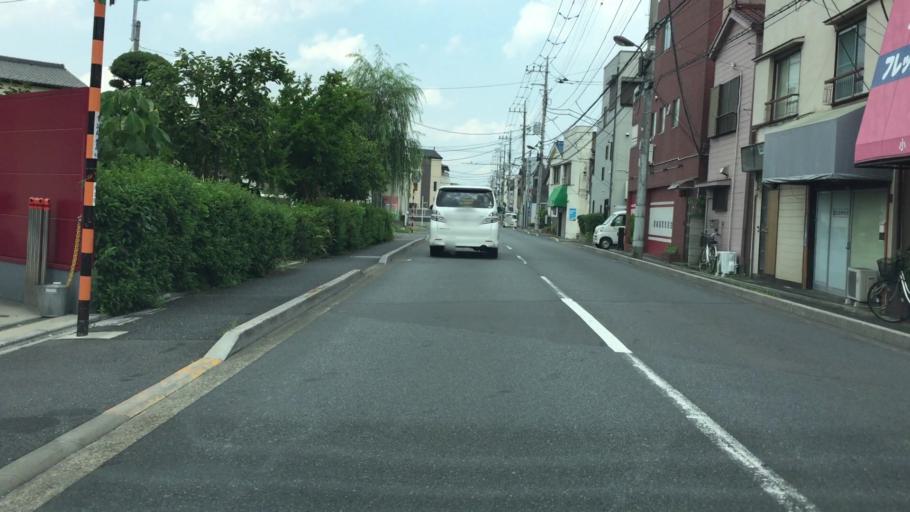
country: JP
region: Saitama
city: Soka
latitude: 35.7738
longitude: 139.8140
